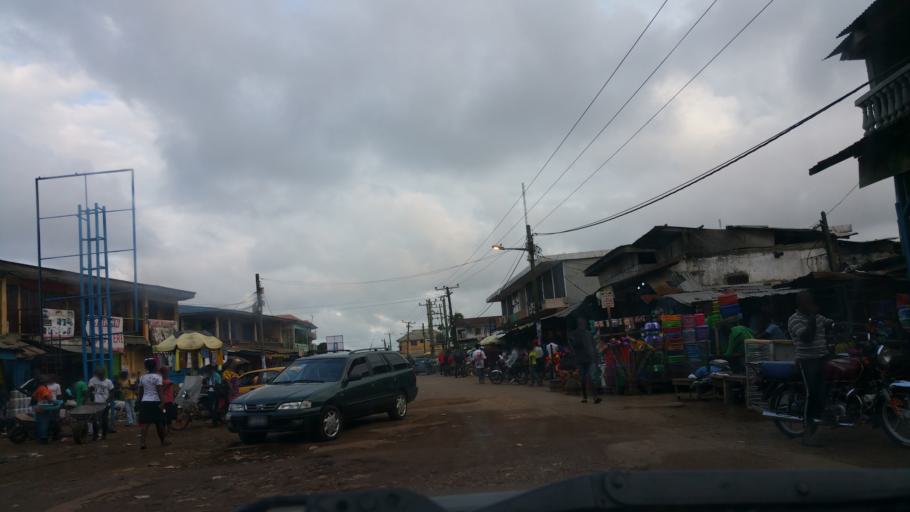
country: LR
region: Montserrado
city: Monrovia
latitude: 6.2802
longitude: -10.7505
